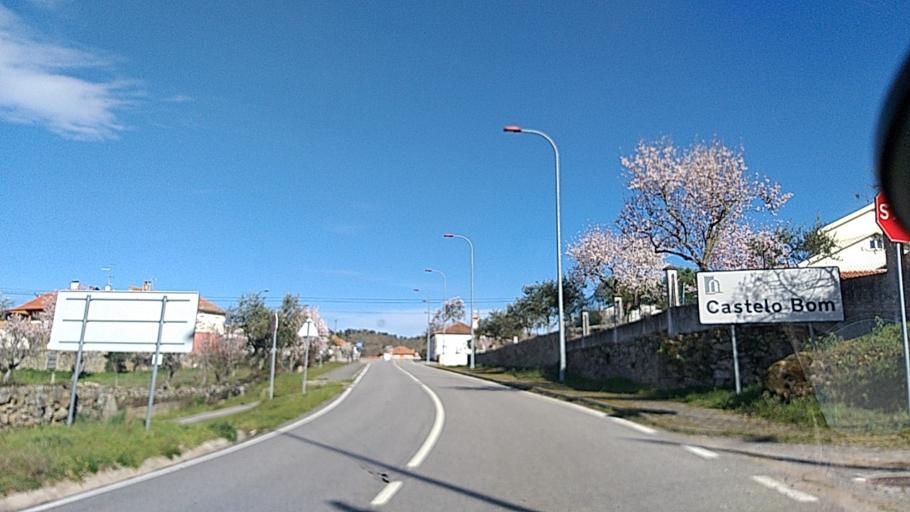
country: ES
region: Castille and Leon
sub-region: Provincia de Salamanca
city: Fuentes de Onoro
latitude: 40.6189
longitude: -6.8999
